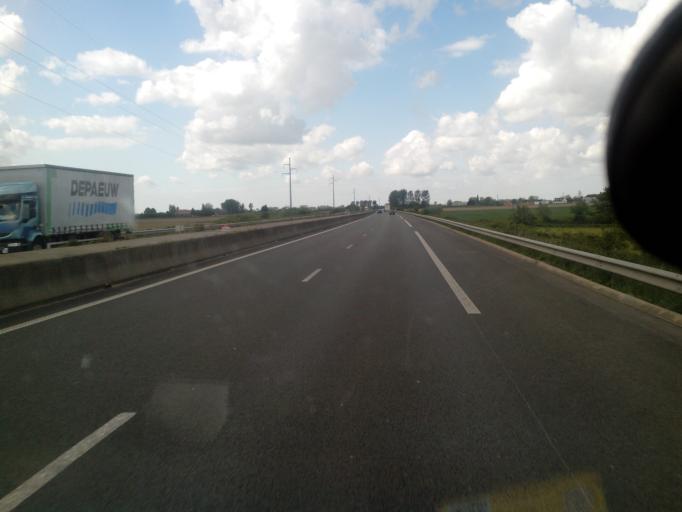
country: FR
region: Nord-Pas-de-Calais
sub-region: Departement du Nord
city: Herzeele
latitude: 50.8969
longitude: 2.5026
